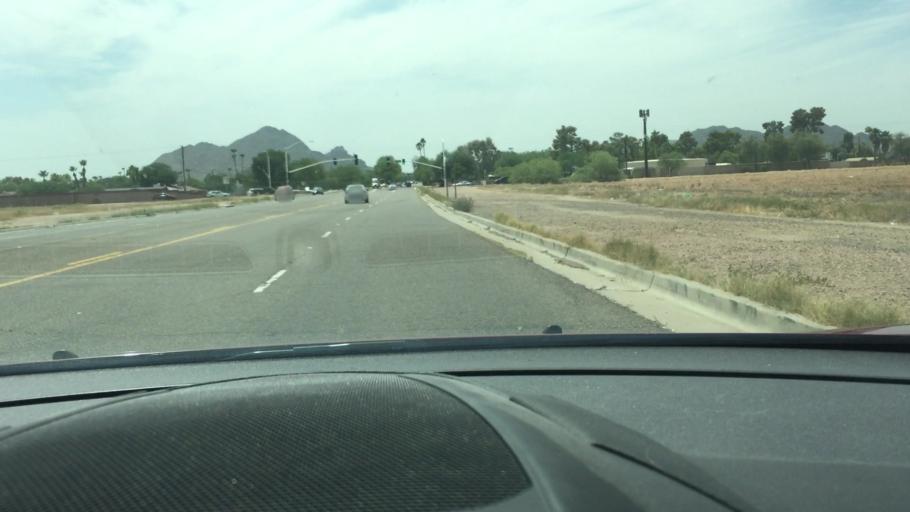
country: US
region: Arizona
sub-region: Maricopa County
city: Scottsdale
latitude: 33.5239
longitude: -111.8894
